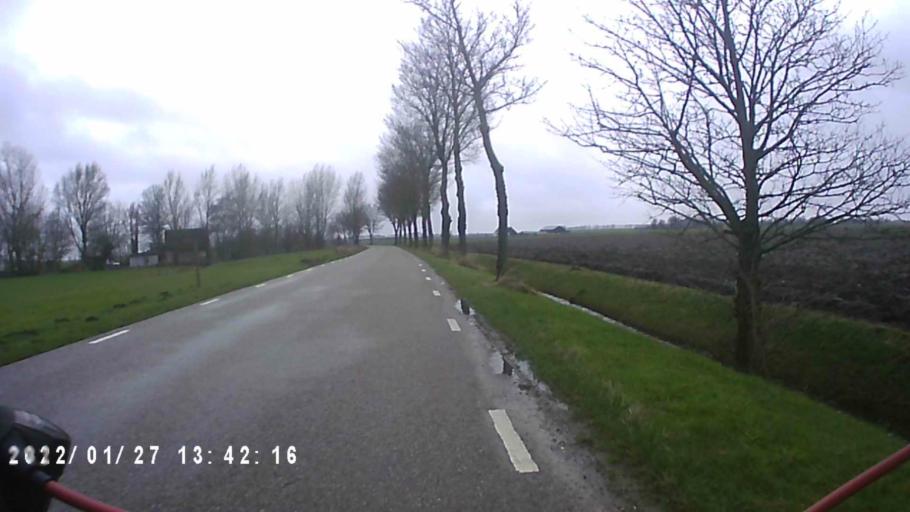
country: NL
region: Friesland
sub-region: Gemeente Kollumerland en Nieuwkruisland
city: Kollum
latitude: 53.3017
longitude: 6.2115
